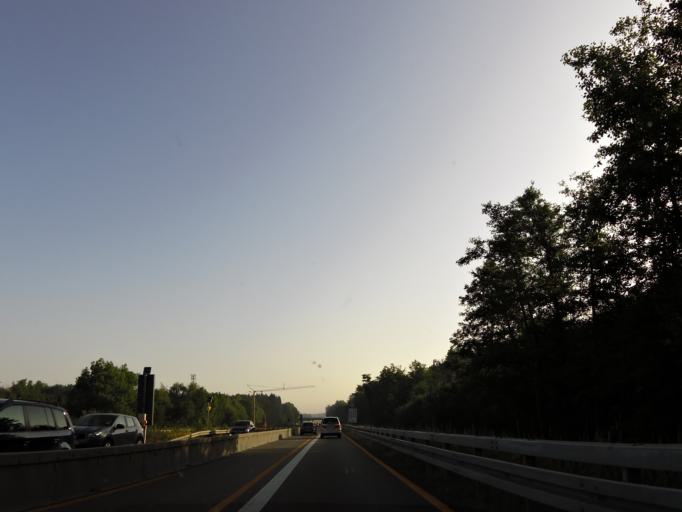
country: DE
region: Bavaria
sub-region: Swabia
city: Holzheim
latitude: 48.3696
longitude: 10.0833
